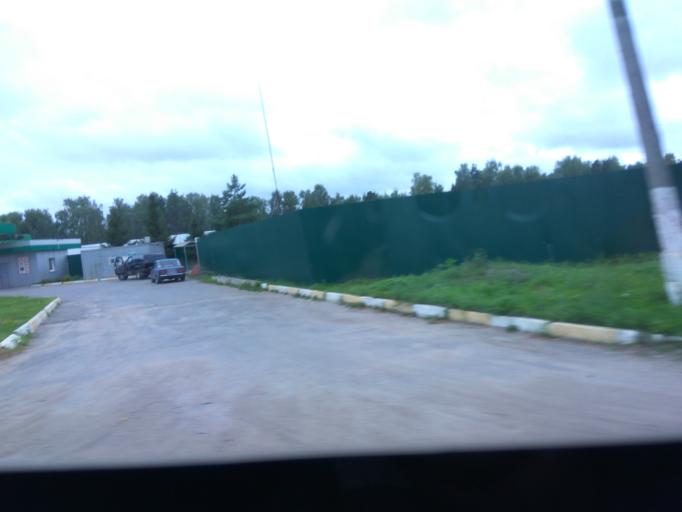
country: RU
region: Moskovskaya
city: Malyshevo
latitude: 55.5147
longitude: 38.3424
